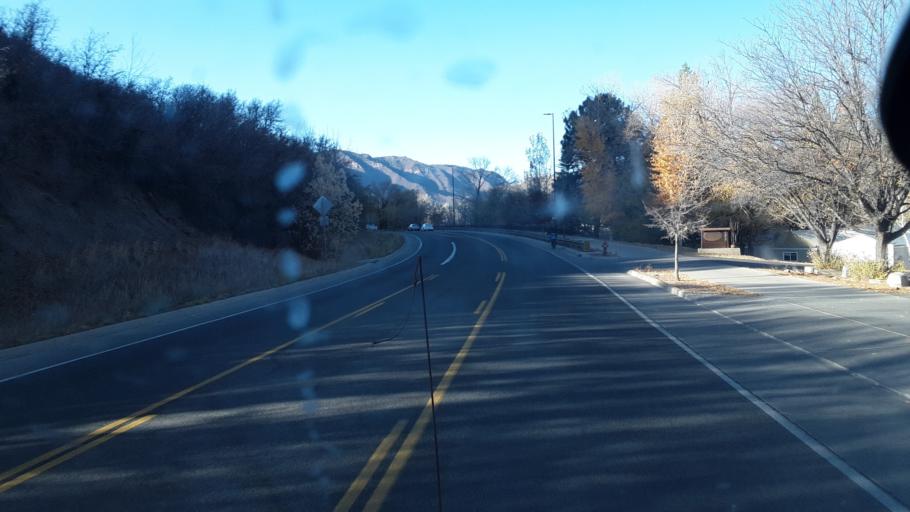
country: US
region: Colorado
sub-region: La Plata County
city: Durango
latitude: 37.2830
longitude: -107.8699
